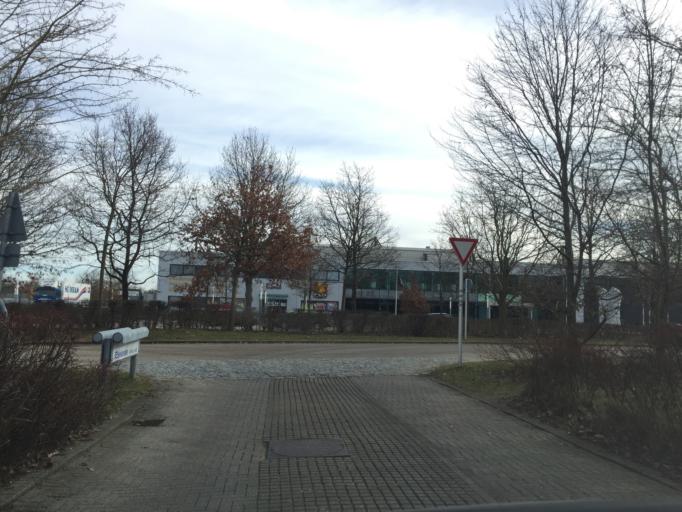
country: DK
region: Capital Region
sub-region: Fureso Kommune
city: Farum
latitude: 55.8163
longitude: 12.3500
